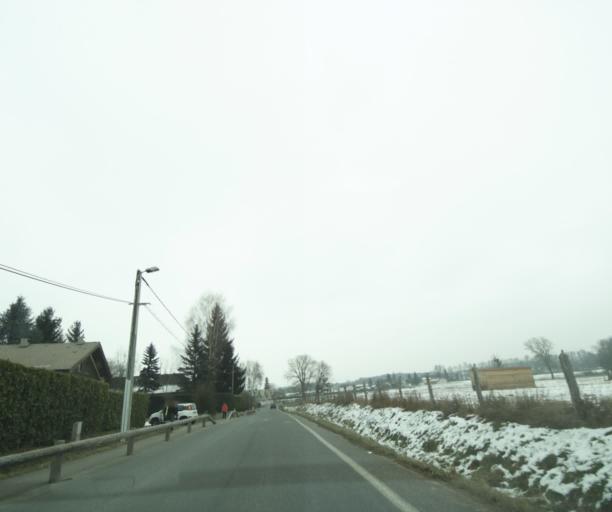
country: FR
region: Rhone-Alpes
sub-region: Departement de la Haute-Savoie
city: Reignier-Esery
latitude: 46.1354
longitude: 6.2769
